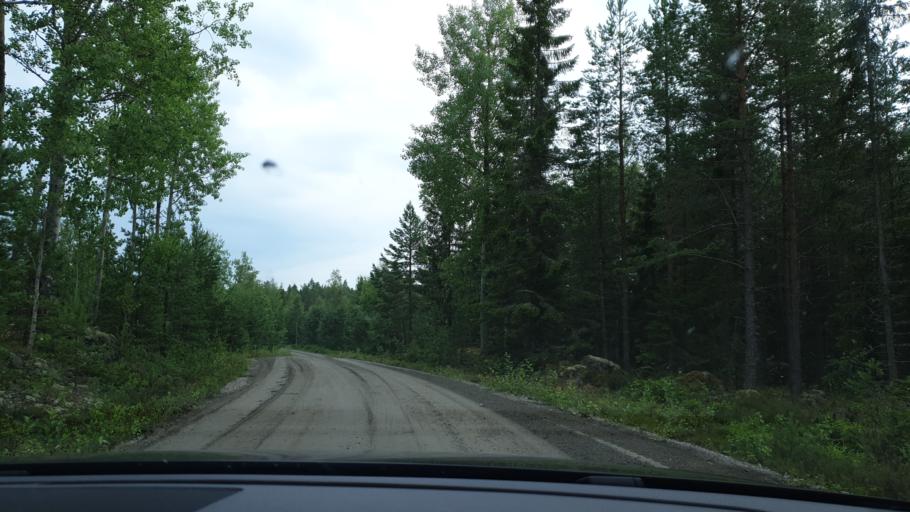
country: SE
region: Gaevleborg
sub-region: Hudiksvalls Kommun
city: Iggesund
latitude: 61.5225
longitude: 17.0159
